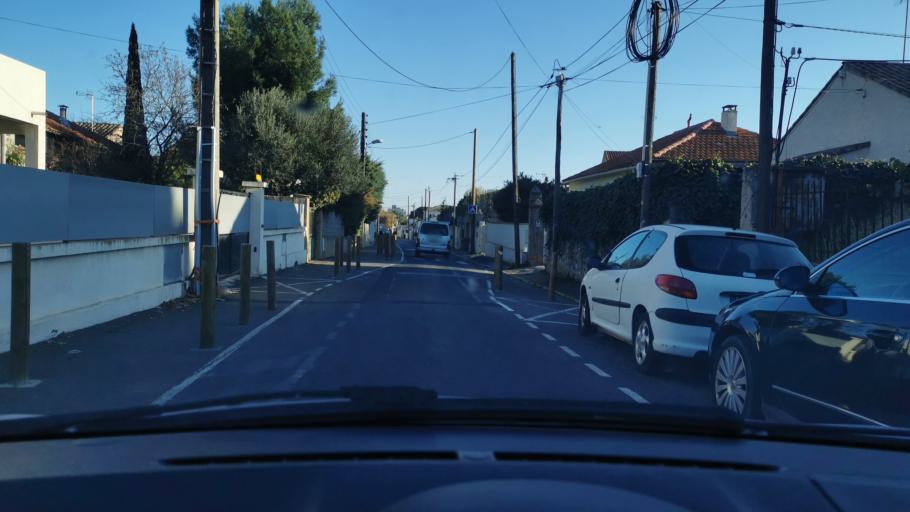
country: FR
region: Languedoc-Roussillon
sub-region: Departement de l'Herault
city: Frontignan
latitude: 43.4502
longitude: 3.7494
